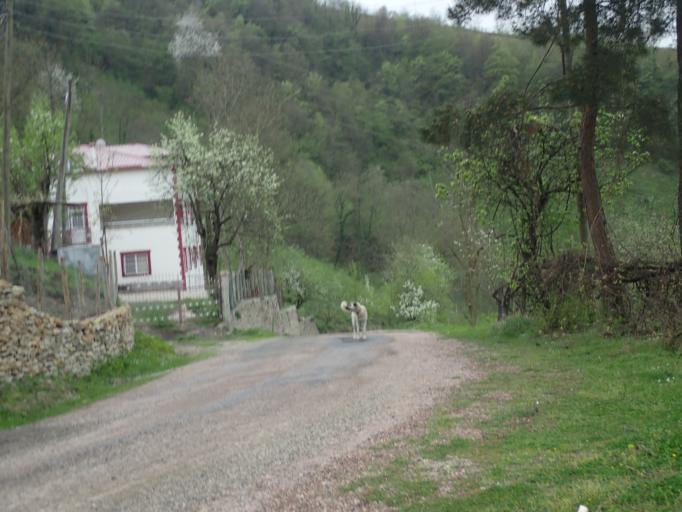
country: TR
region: Ordu
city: Korgan
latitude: 40.7801
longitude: 37.3464
